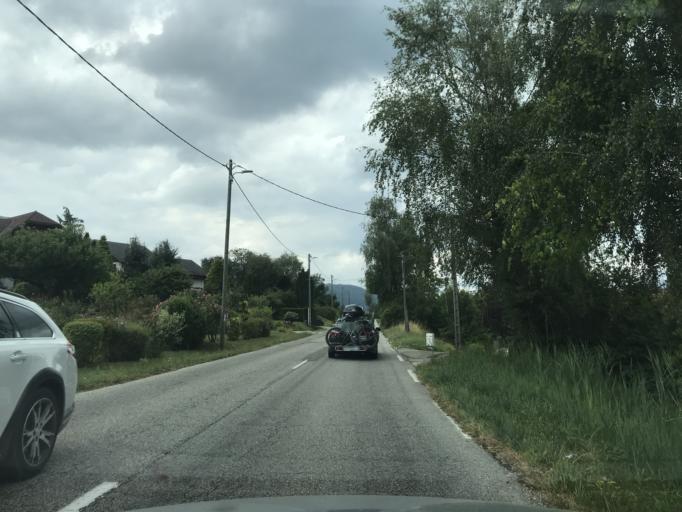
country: FR
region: Rhone-Alpes
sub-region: Departement de la Savoie
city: Brison-Saint-Innocent
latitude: 45.7326
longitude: 5.8870
